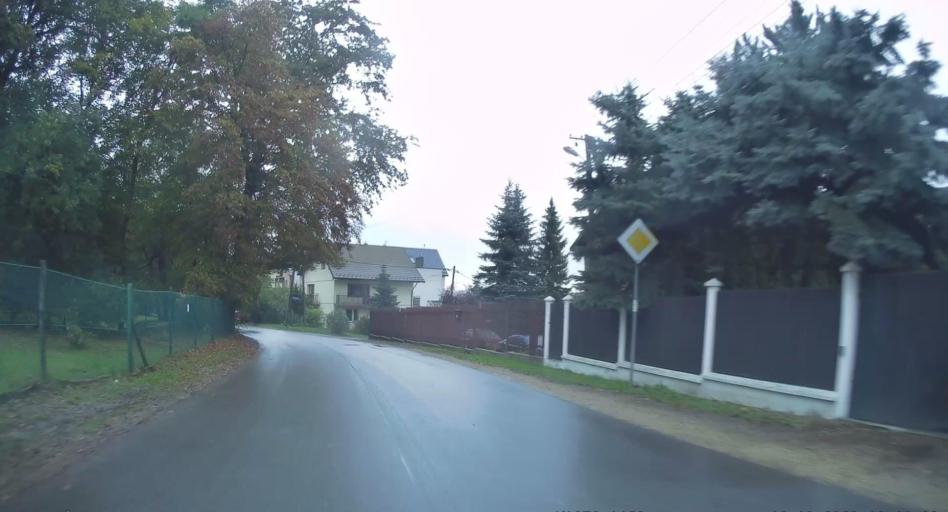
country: PL
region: Lesser Poland Voivodeship
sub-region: Powiat krakowski
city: Ochojno
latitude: 50.0078
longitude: 19.9828
